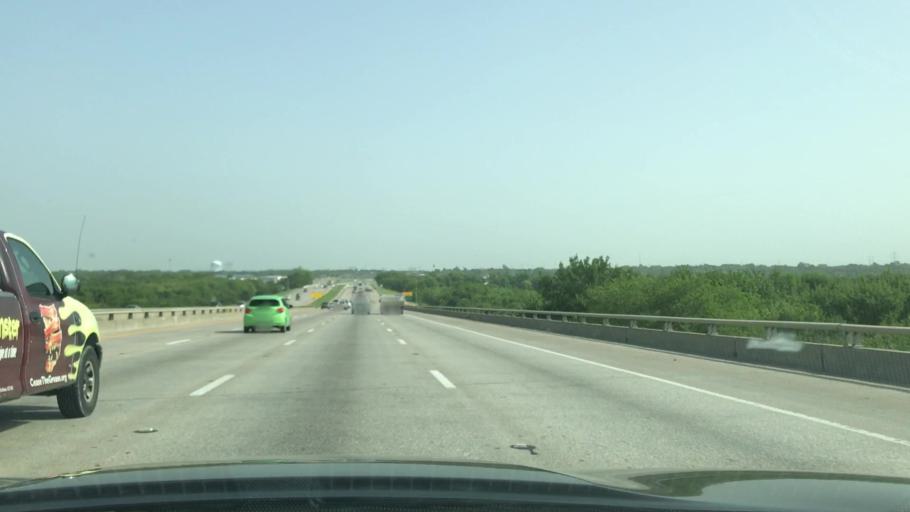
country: US
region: Texas
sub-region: Dallas County
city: Irving
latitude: 32.7879
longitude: -96.9190
